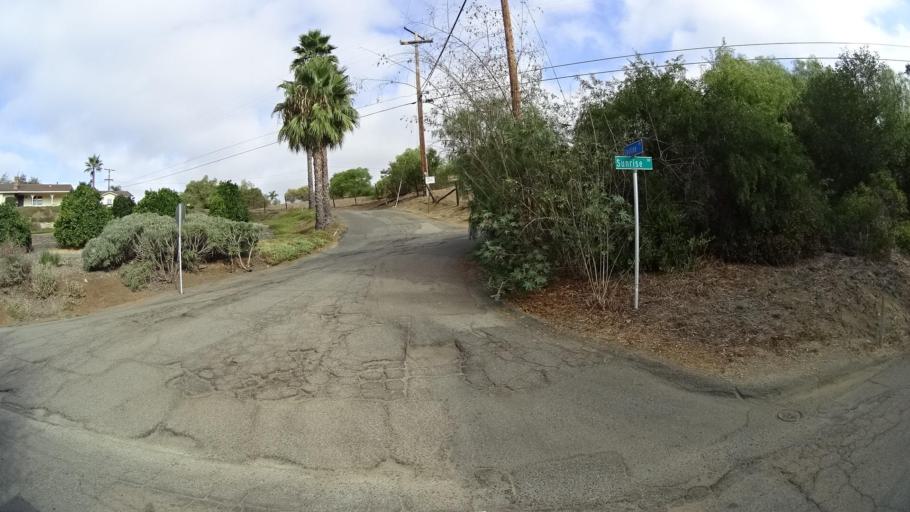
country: US
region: California
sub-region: San Diego County
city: Vista
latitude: 33.2009
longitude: -117.2118
